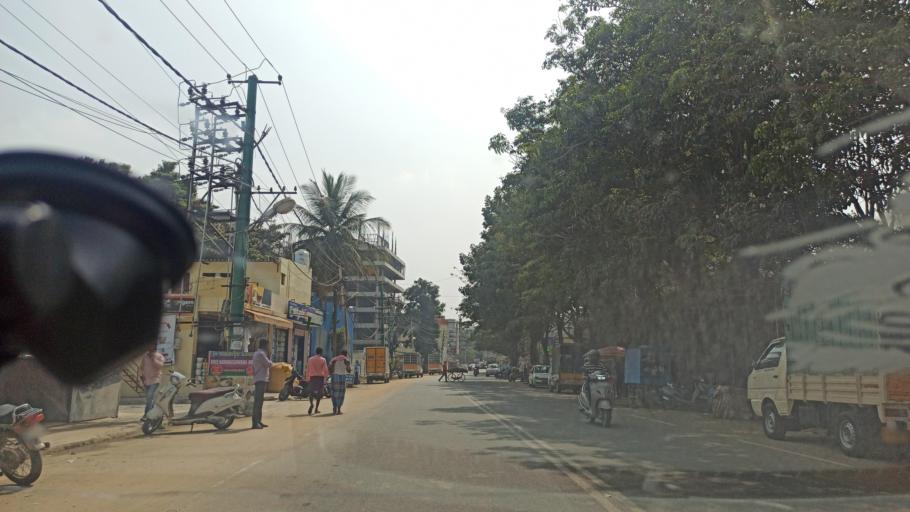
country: IN
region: Karnataka
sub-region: Bangalore Urban
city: Yelahanka
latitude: 13.0947
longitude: 77.6007
